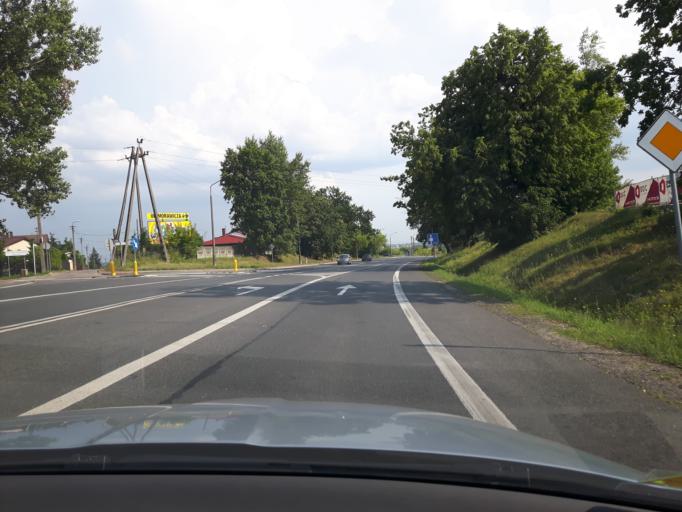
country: PL
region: Masovian Voivodeship
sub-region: Powiat nowodworski
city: Nowy Dwor Mazowiecki
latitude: 52.4451
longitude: 20.6948
